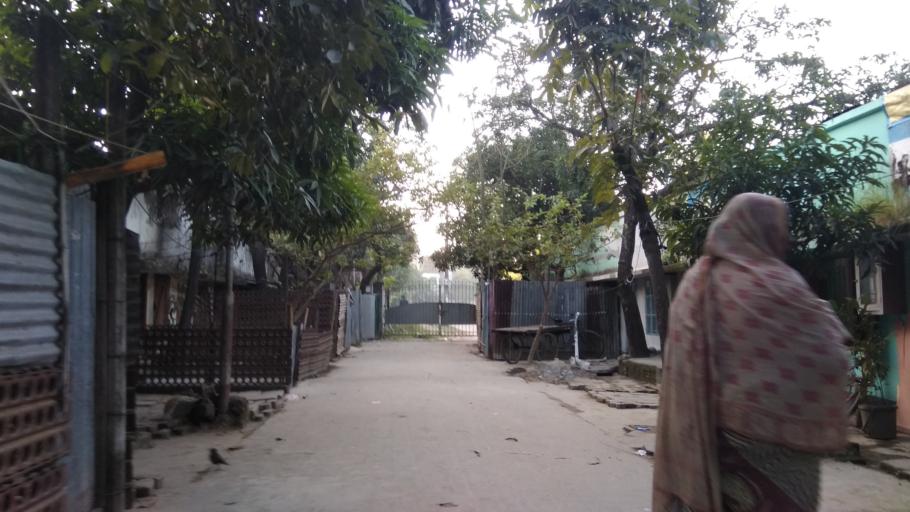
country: BD
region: Dhaka
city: Tungi
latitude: 23.8434
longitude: 90.4214
